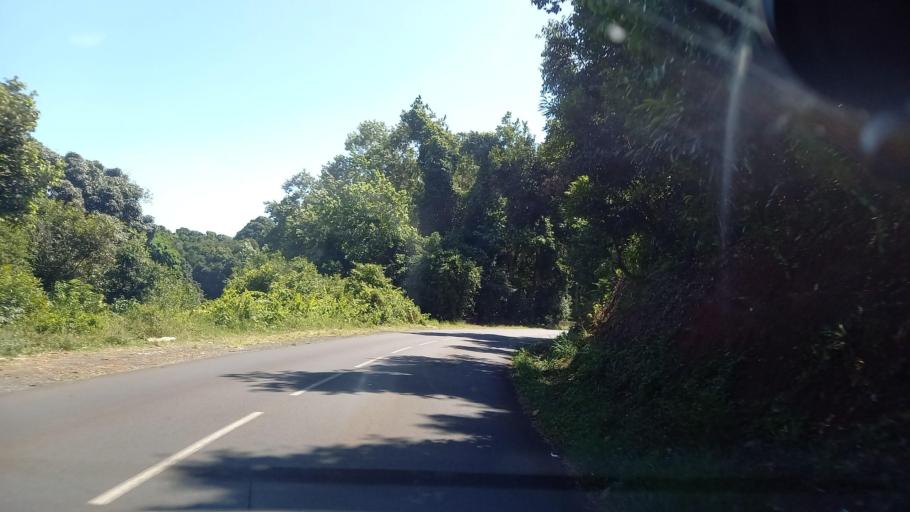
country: YT
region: Tsingoni
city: Tsingoni
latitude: -12.7875
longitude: 45.1546
